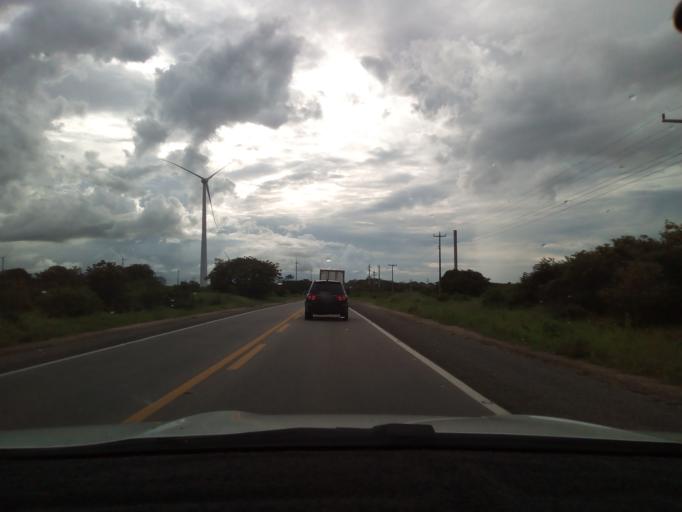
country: BR
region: Ceara
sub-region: Aracati
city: Aracati
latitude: -4.5948
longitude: -37.6823
